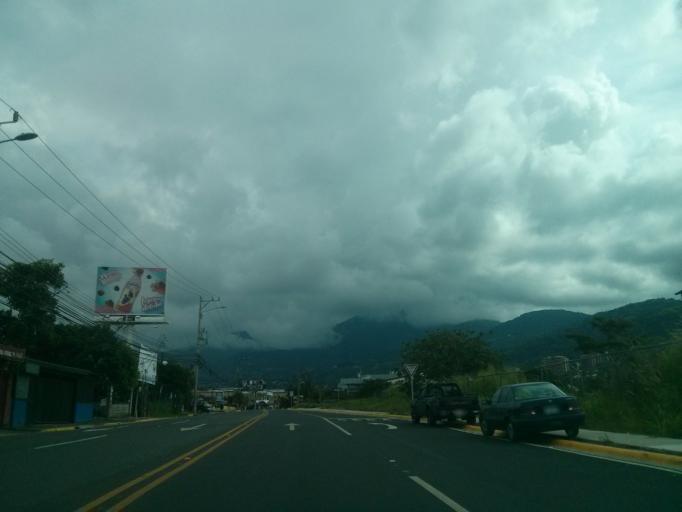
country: CR
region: San Jose
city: San Rafael
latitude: 9.9415
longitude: -84.1521
